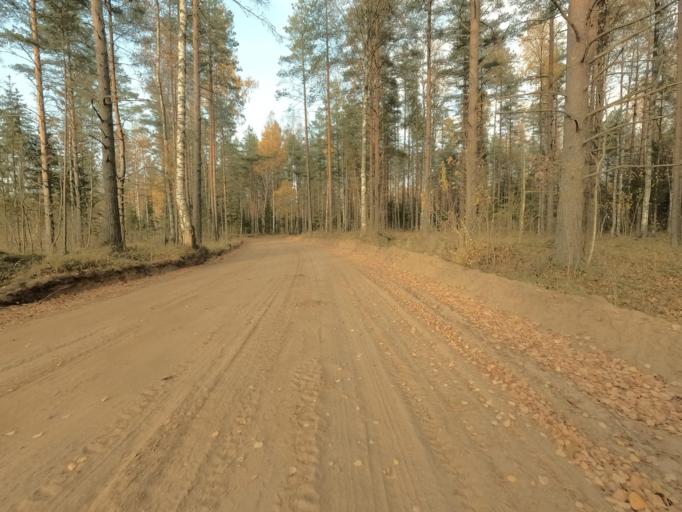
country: RU
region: Leningrad
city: Priladozhskiy
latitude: 59.7375
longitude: 31.3173
